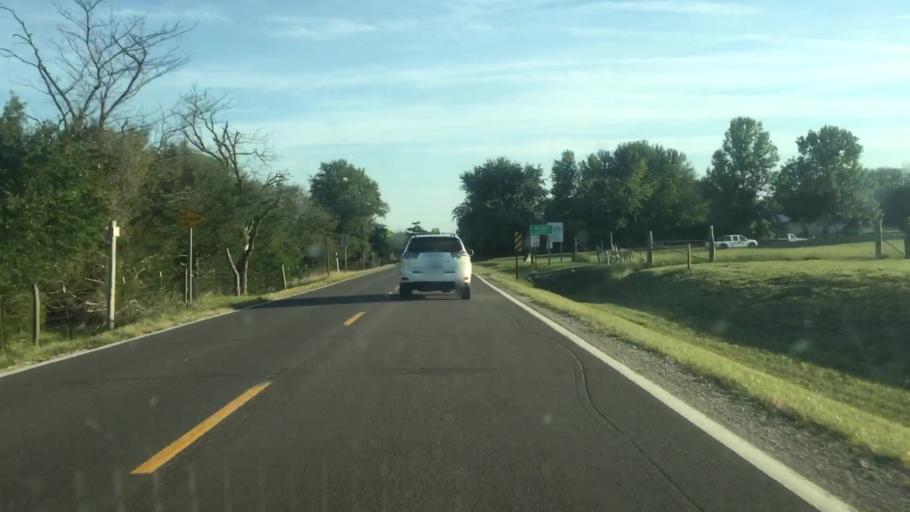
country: US
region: Kansas
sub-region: Brown County
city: Horton
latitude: 39.5580
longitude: -95.5247
